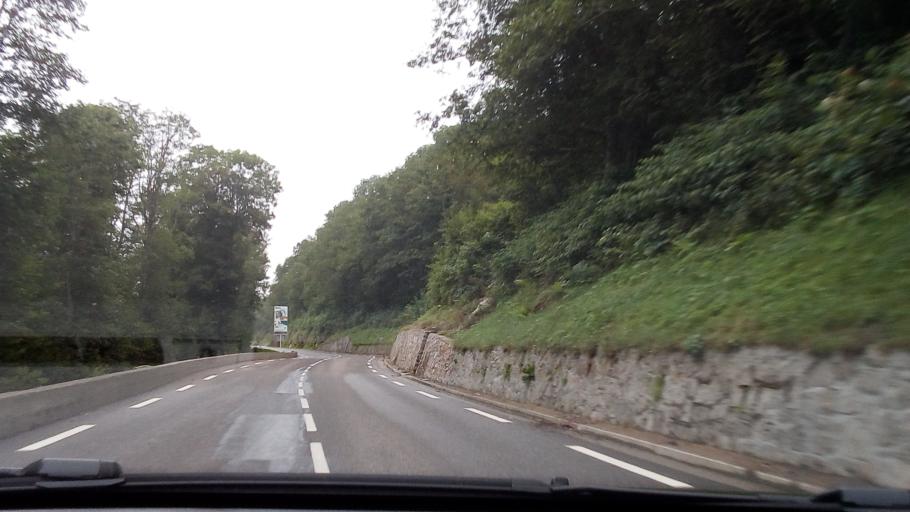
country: FR
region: Midi-Pyrenees
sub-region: Departement des Hautes-Pyrenees
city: Luz-Saint-Sauveur
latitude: 42.8995
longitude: 0.0772
